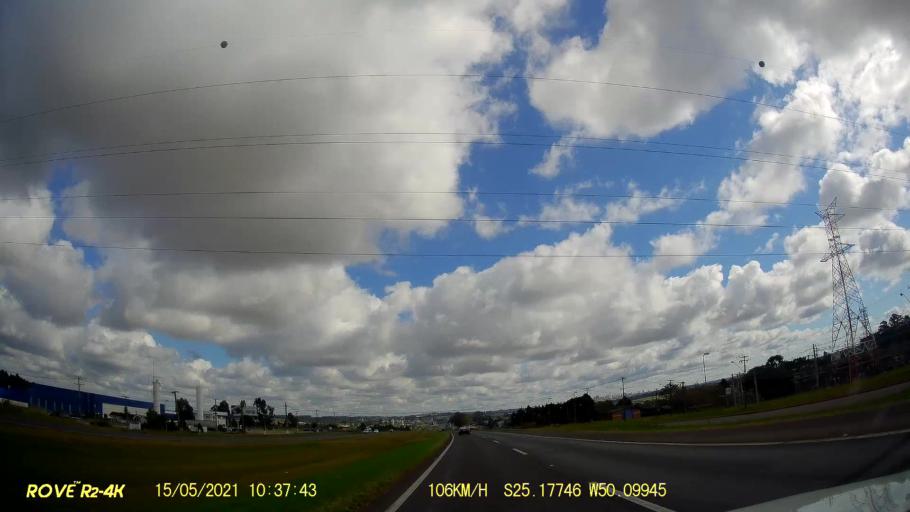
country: BR
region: Parana
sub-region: Ponta Grossa
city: Ponta Grossa
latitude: -25.1775
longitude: -50.0994
